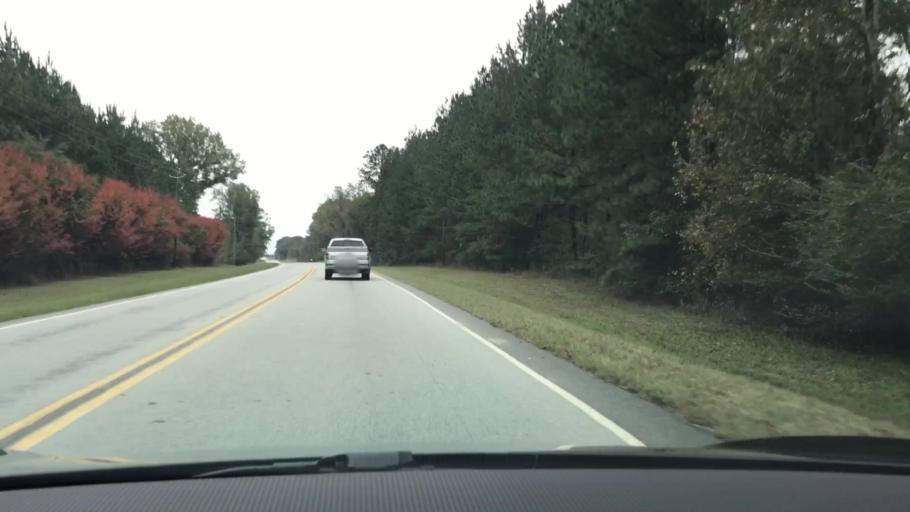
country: US
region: Georgia
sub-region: Warren County
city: Firing Range
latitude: 33.4398
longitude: -82.6913
